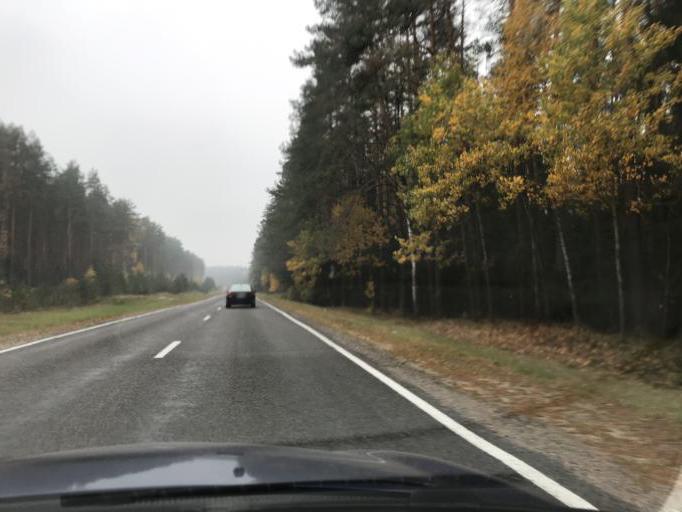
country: LT
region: Alytaus apskritis
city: Druskininkai
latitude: 53.8759
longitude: 23.8993
